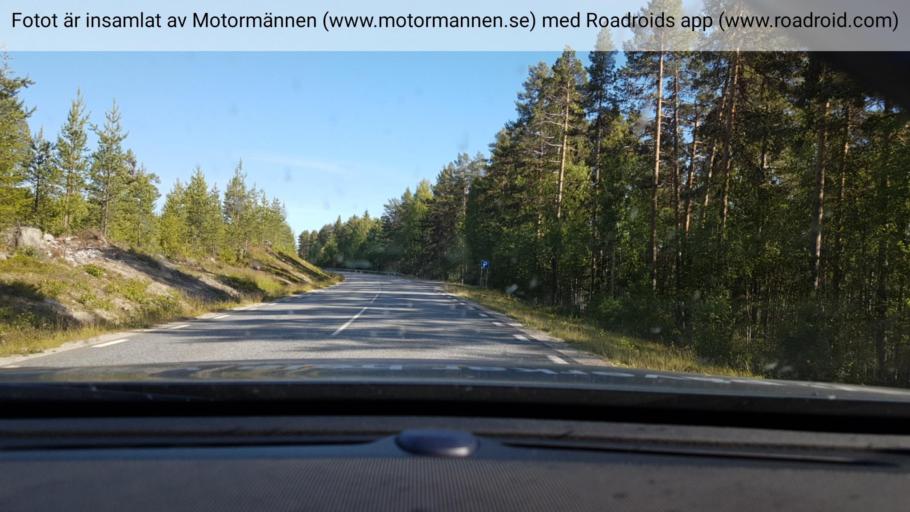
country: SE
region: Vaesterbotten
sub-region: Lycksele Kommun
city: Lycksele
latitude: 64.4432
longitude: 18.9430
